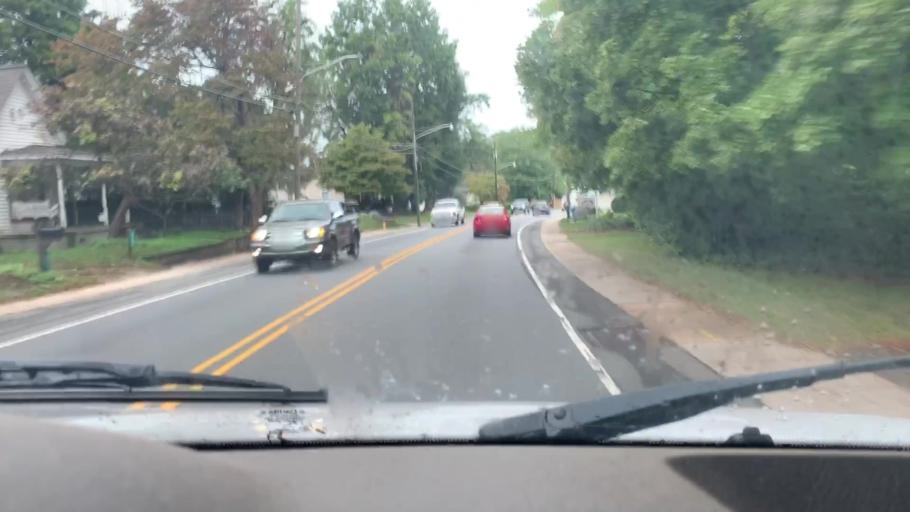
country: US
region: North Carolina
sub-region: Mecklenburg County
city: Cornelius
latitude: 35.4843
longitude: -80.8588
